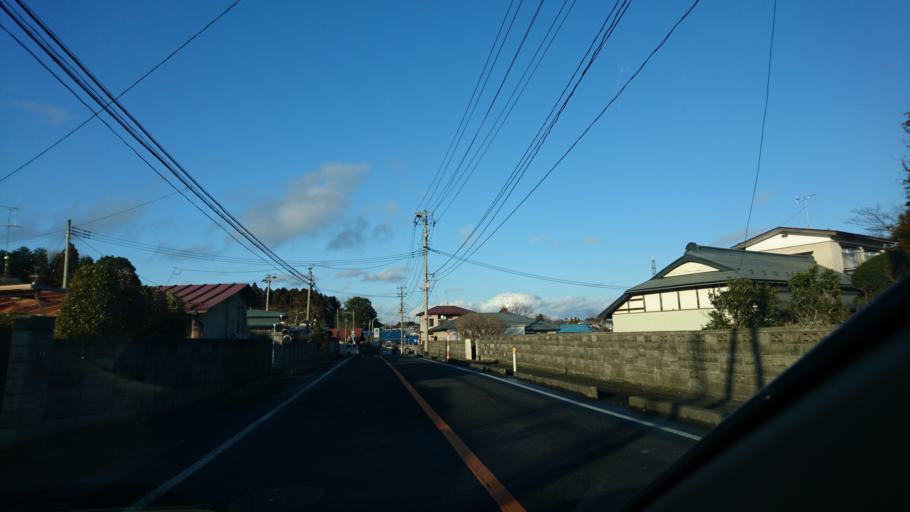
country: JP
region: Miyagi
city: Furukawa
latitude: 38.5887
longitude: 140.8604
